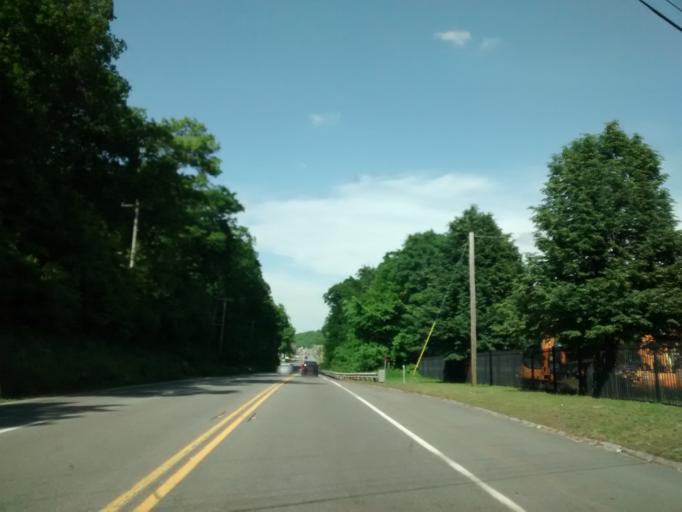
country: US
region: Massachusetts
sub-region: Worcester County
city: Shrewsbury
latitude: 42.2730
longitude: -71.6829
